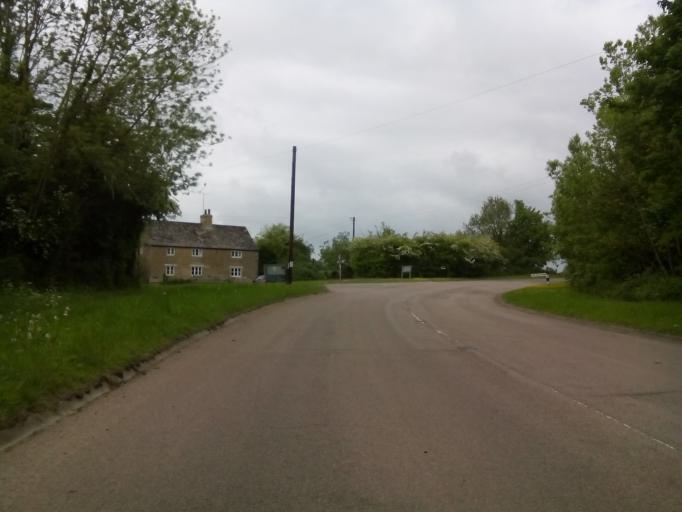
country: GB
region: England
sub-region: District of Rutland
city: South Luffenham
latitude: 52.5393
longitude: -0.5856
